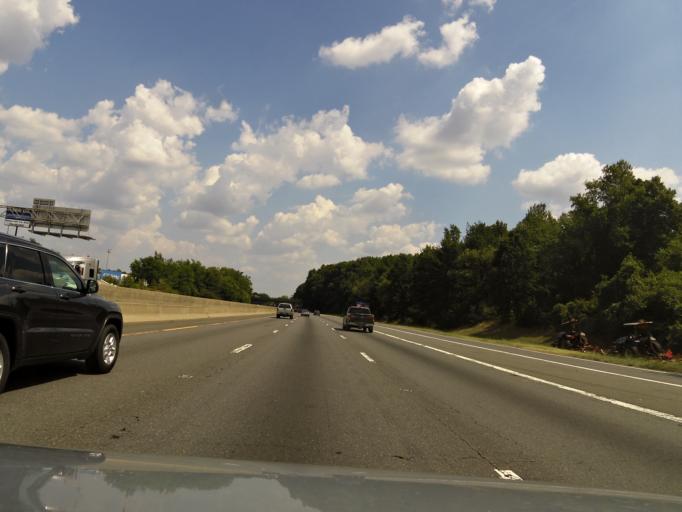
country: US
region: North Carolina
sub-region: Gaston County
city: Ranlo
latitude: 35.2676
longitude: -81.1469
